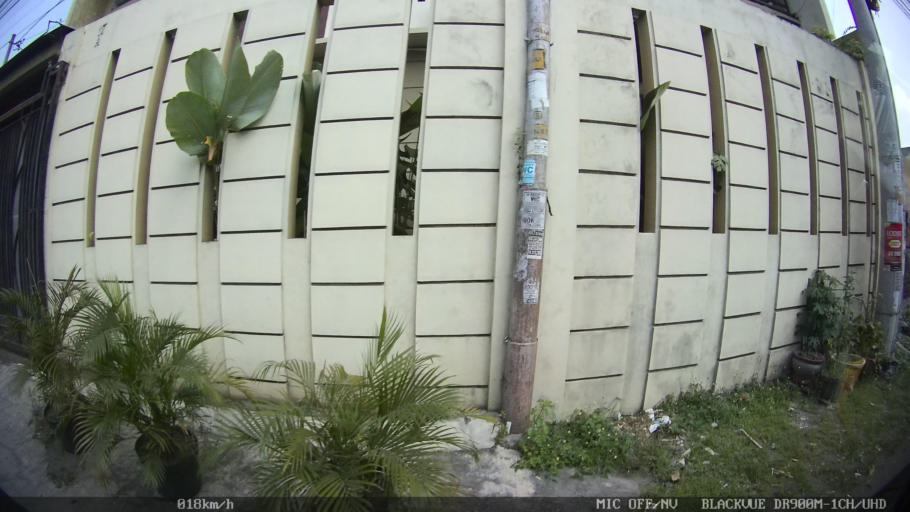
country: ID
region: Daerah Istimewa Yogyakarta
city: Yogyakarta
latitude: -7.7982
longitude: 110.3941
